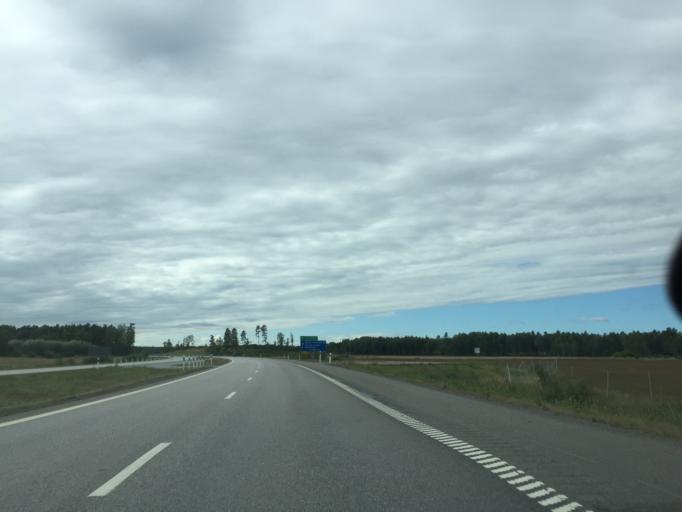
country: SE
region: Vaestmanland
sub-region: Arboga Kommun
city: Arboga
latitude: 59.4210
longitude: 15.7811
